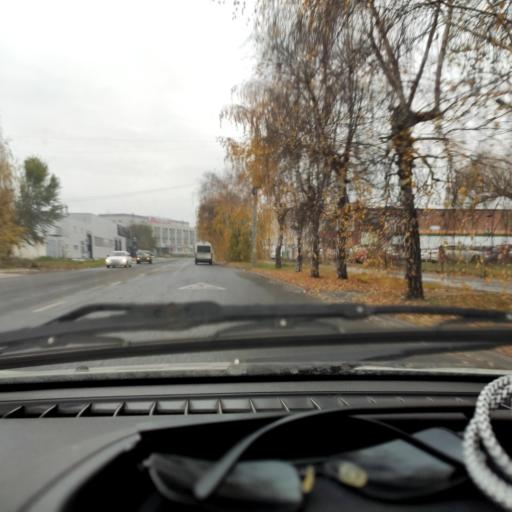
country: RU
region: Samara
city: Tol'yatti
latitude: 53.5313
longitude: 49.4306
